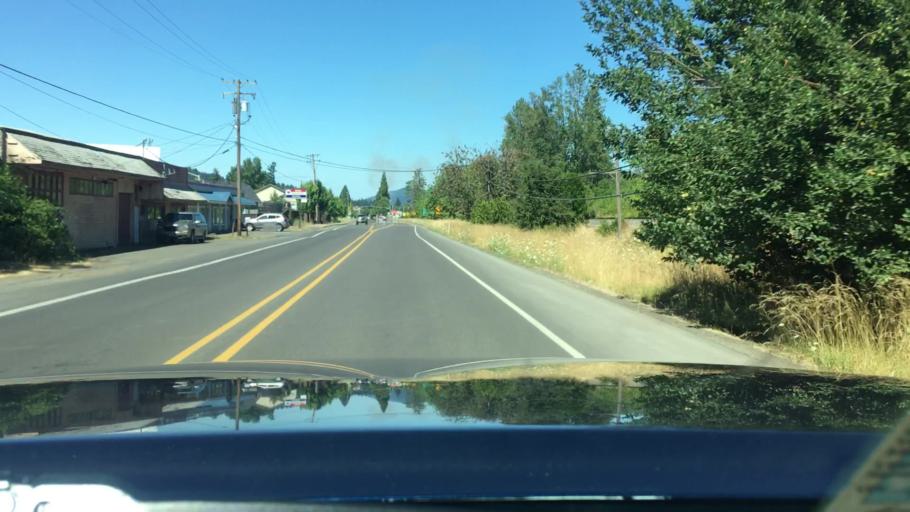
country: US
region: Oregon
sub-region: Lane County
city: Cottage Grove
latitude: 43.7858
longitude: -123.0672
